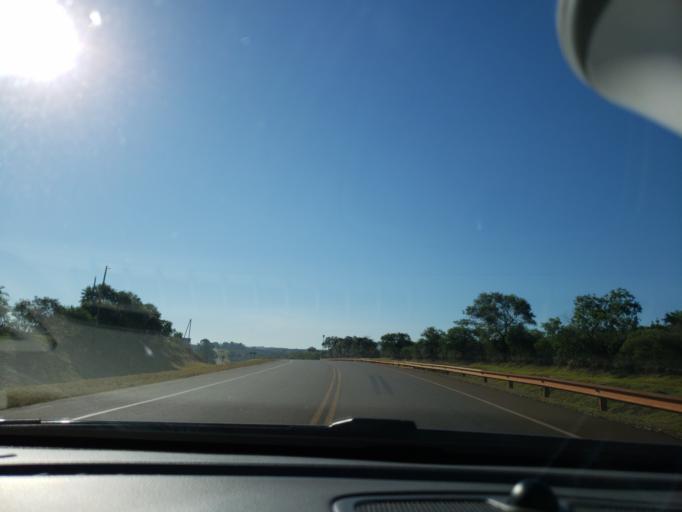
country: AR
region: Misiones
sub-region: Departamento de Apostoles
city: Apostoles
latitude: -27.8525
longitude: -55.7631
